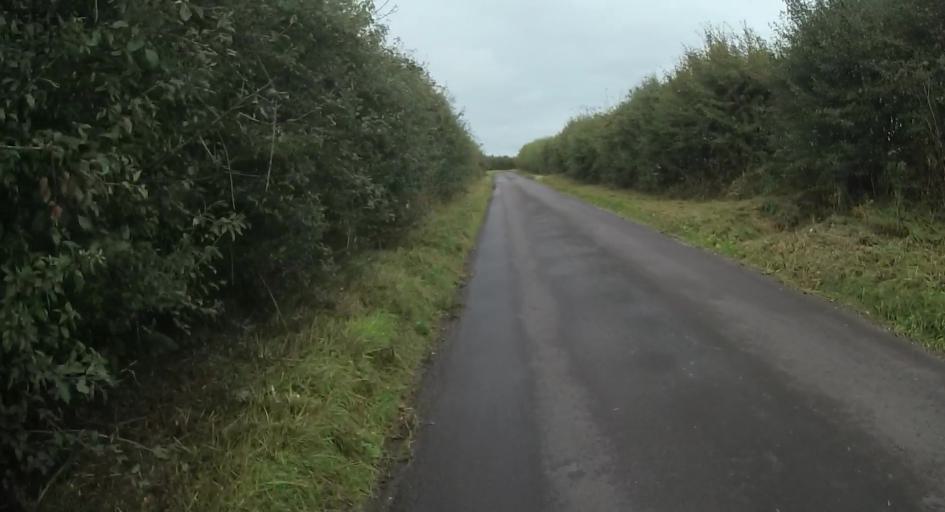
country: GB
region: England
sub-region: Hampshire
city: Basingstoke
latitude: 51.2794
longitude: -1.1464
